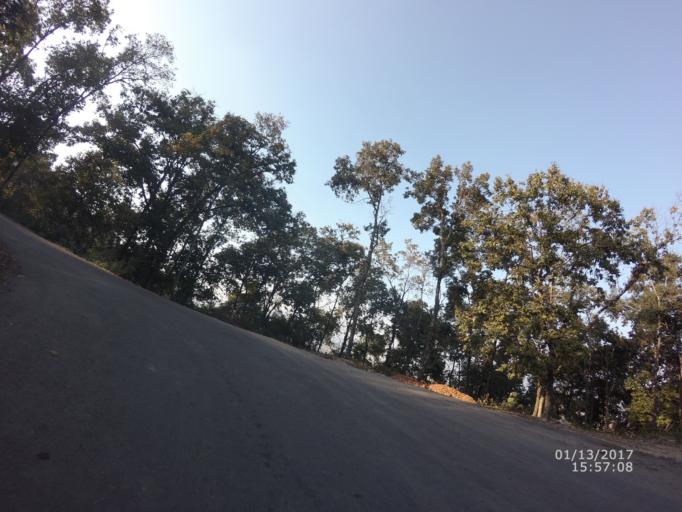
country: NP
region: Western Region
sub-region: Gandaki Zone
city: Pokhara
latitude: 28.1616
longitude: 84.0025
